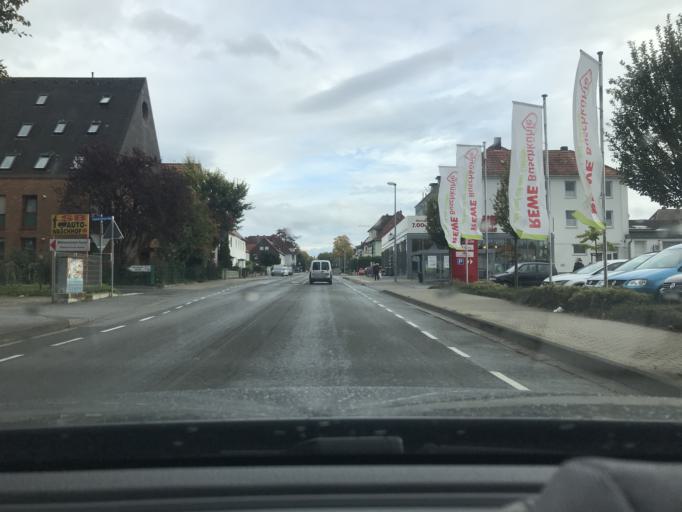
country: DE
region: North Rhine-Westphalia
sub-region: Regierungsbezirk Arnsberg
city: Soest
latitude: 51.5634
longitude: 8.1203
